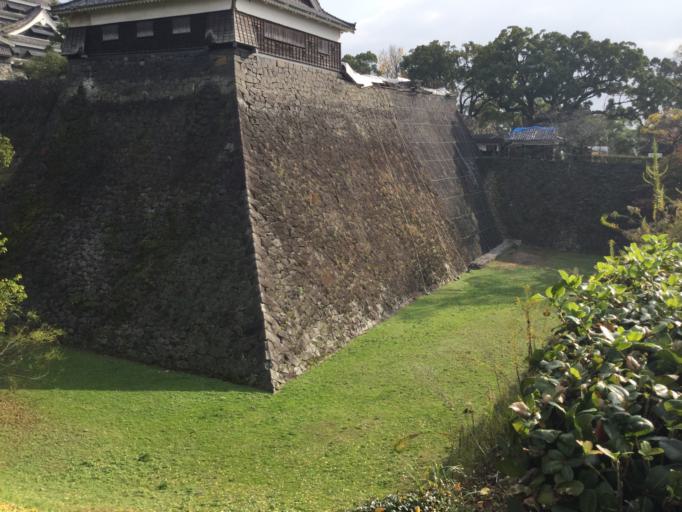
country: JP
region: Kumamoto
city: Kumamoto
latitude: 32.8069
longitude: 130.7044
